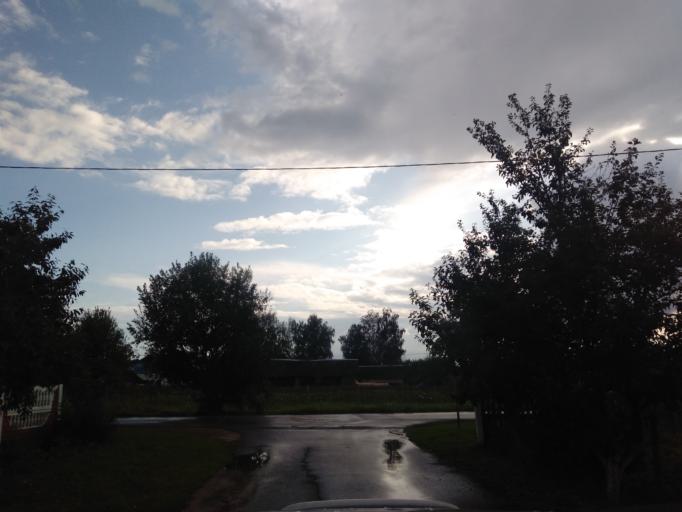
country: BY
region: Minsk
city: Kapyl'
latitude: 53.1601
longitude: 27.0738
